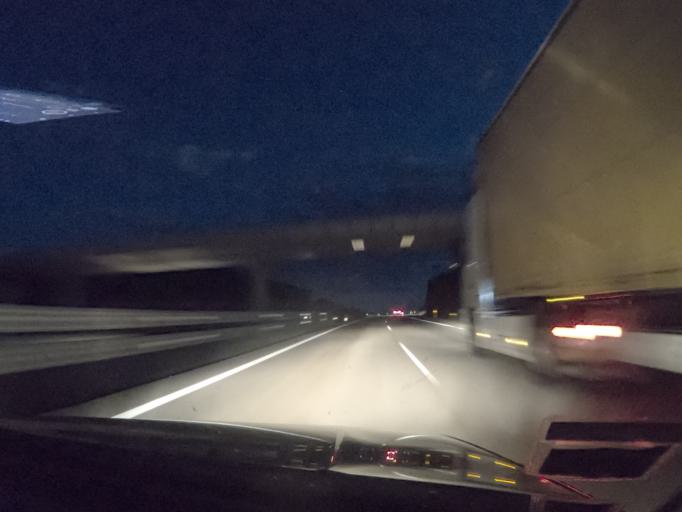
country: ES
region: Castille and Leon
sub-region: Provincia de Leon
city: Brazuelo
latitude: 42.5089
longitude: -6.1169
